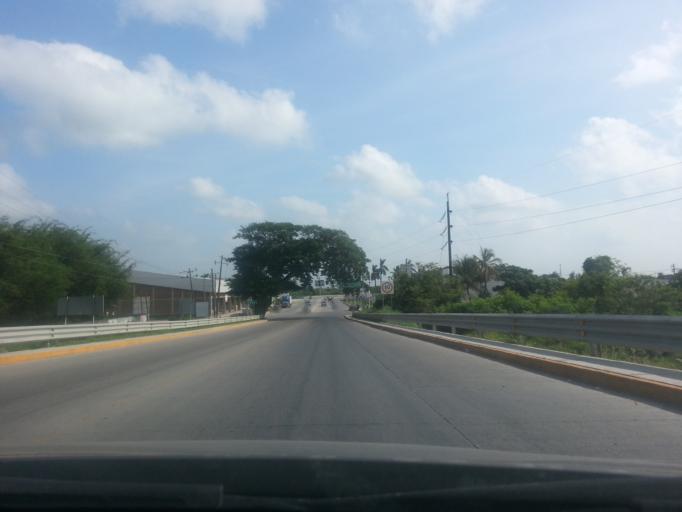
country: MX
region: Veracruz
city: Tuxpan de Rodriguez Cano
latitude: 20.9461
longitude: -97.4008
